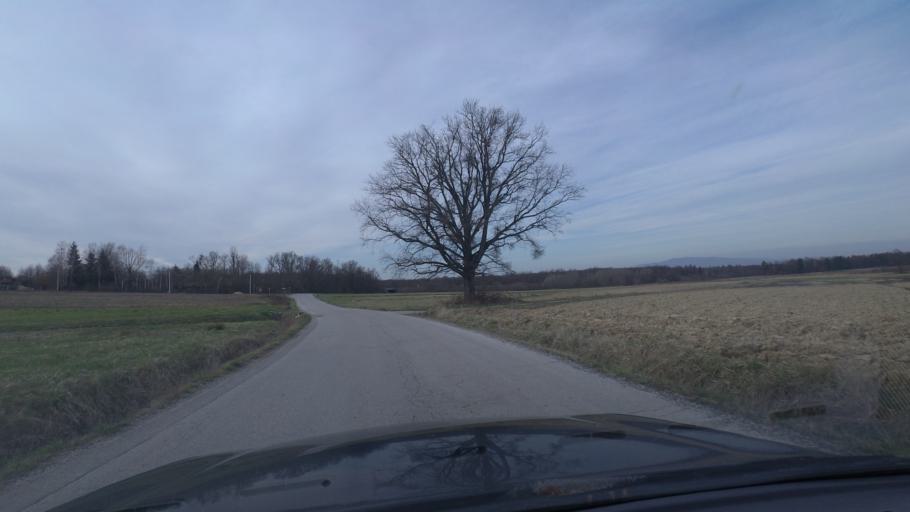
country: HR
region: Grad Zagreb
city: Horvati
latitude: 45.6952
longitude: 15.8386
